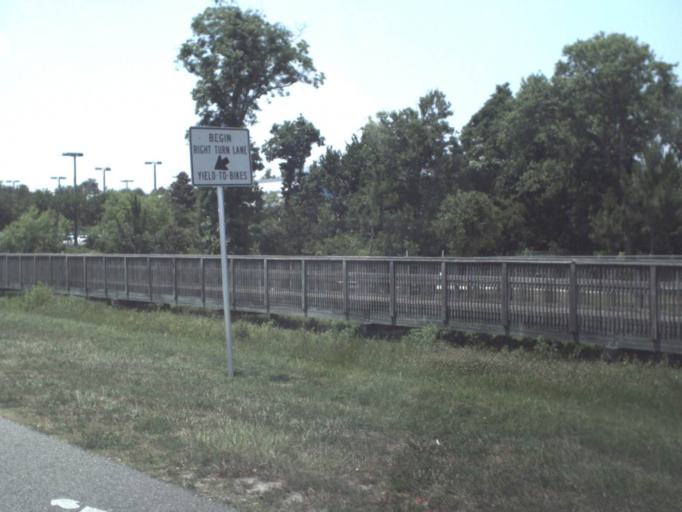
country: US
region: Florida
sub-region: Saint Johns County
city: Saint Augustine South
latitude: 29.8412
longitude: -81.3225
